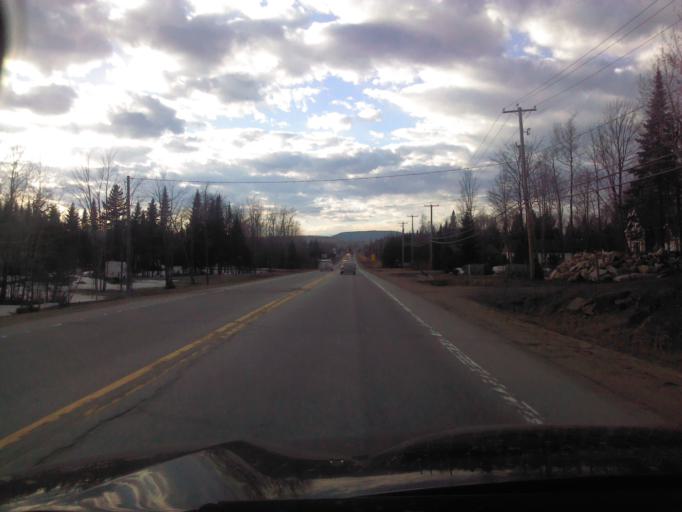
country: CA
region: Quebec
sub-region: Capitale-Nationale
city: Sainte Catherine de la Jacques Cartier
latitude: 46.8302
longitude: -71.5965
